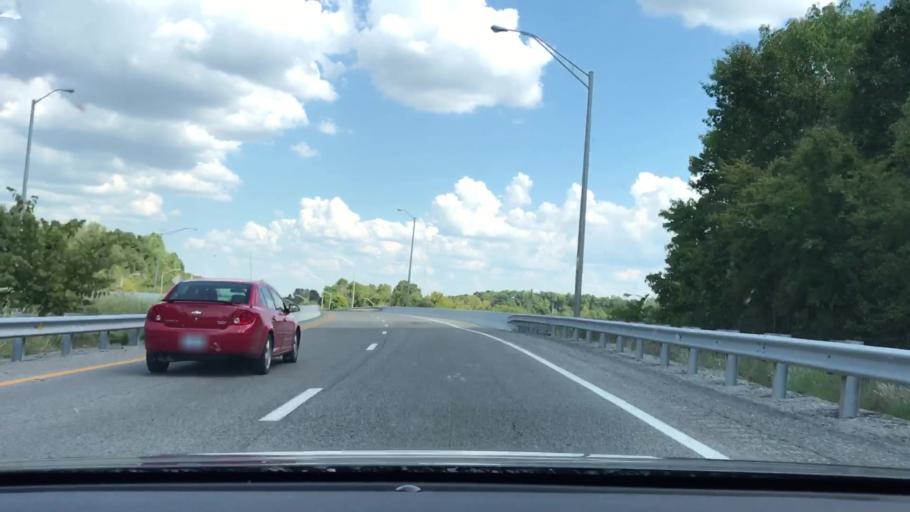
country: US
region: Kentucky
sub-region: Lyon County
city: Eddyville
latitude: 37.0709
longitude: -88.0856
